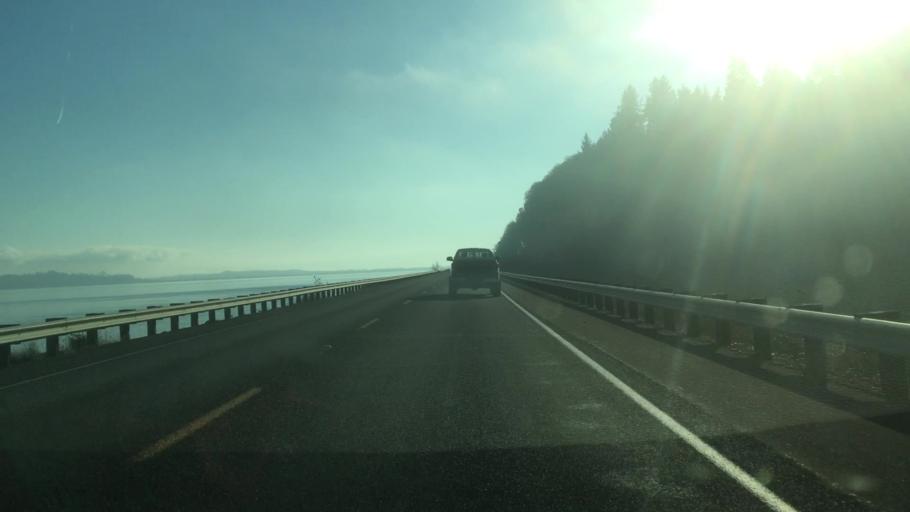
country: US
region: Oregon
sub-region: Clatsop County
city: Astoria
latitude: 46.2667
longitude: -123.8360
